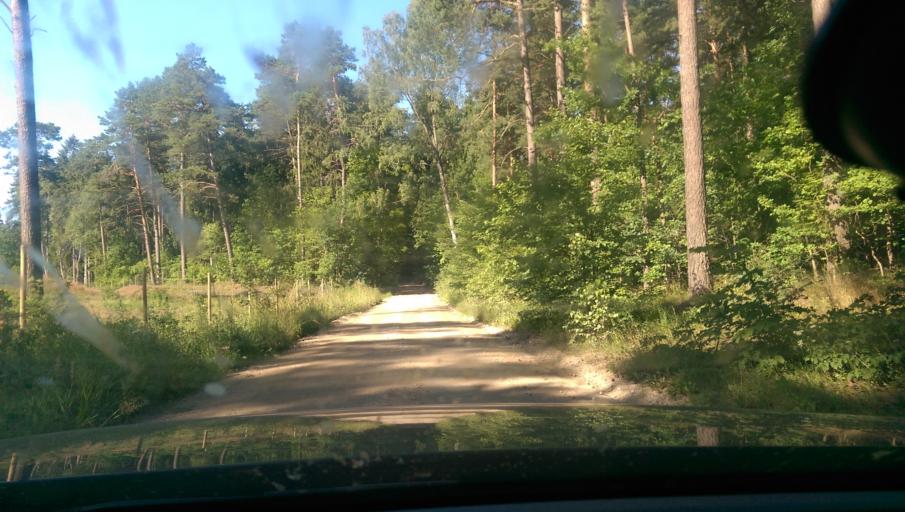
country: LT
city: Priekule
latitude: 55.6502
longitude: 21.3253
